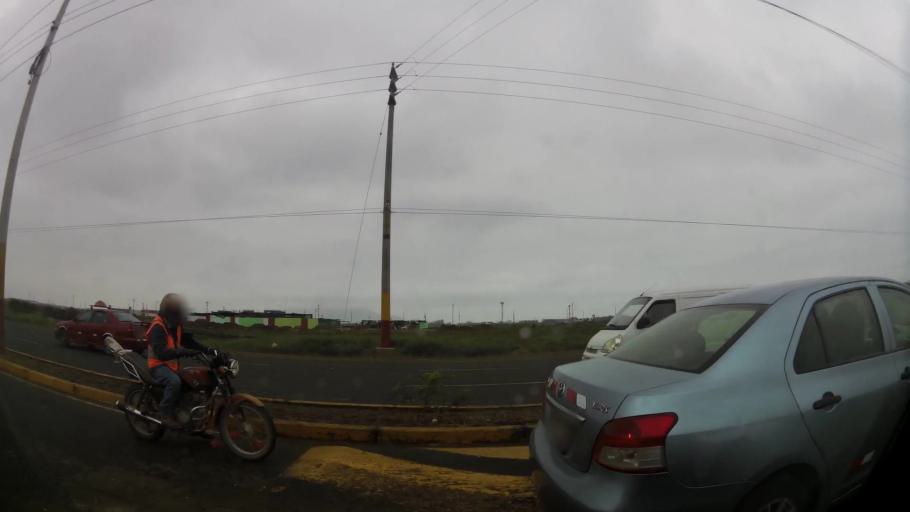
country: PE
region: Ancash
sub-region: Provincia de Santa
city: Chimbote
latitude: -9.1053
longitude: -78.5526
